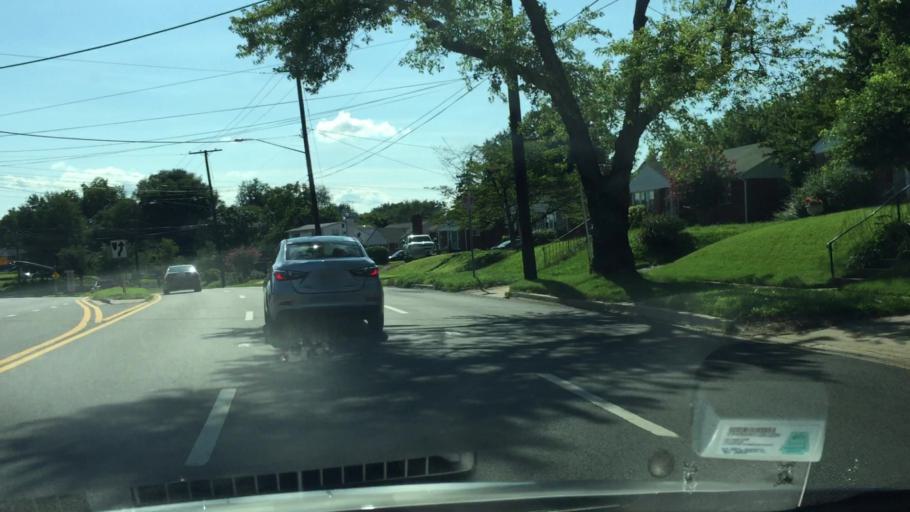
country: US
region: Maryland
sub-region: Montgomery County
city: Glenmont
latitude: 39.0592
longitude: -77.0695
